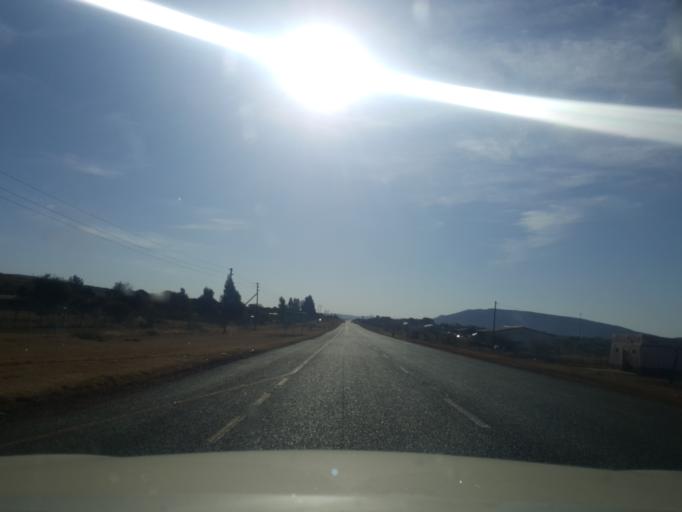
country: ZA
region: North-West
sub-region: Ngaka Modiri Molema District Municipality
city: Zeerust
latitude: -25.4730
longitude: 25.8996
